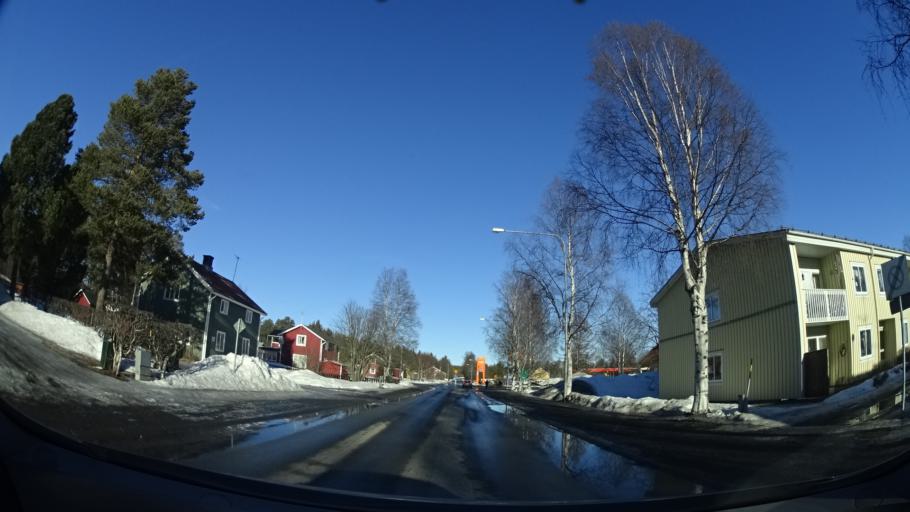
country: SE
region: Vaesterbotten
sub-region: Skelleftea Kommun
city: Byske
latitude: 64.9559
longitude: 21.2076
